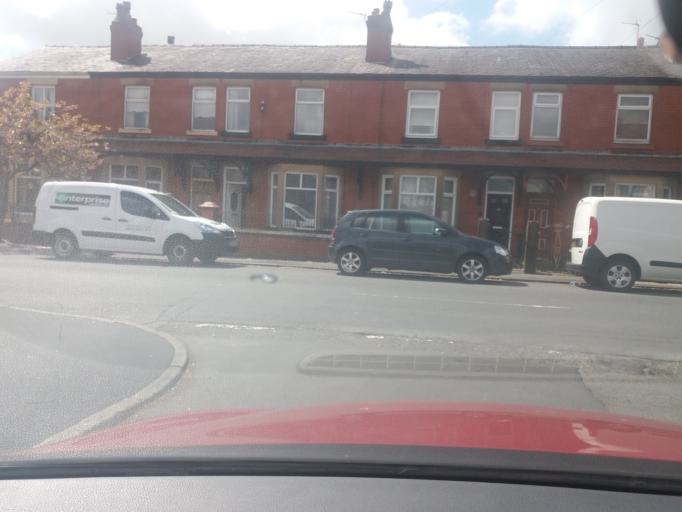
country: GB
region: England
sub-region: Lancashire
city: Chorley
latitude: 53.6430
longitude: -2.6363
